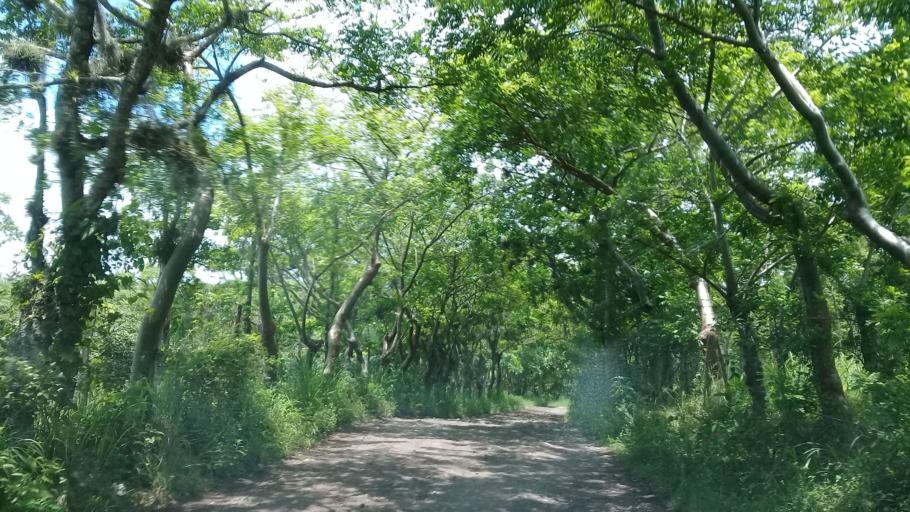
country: MX
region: Veracruz
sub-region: Naolinco
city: El Espinal
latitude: 19.5919
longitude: -96.8729
